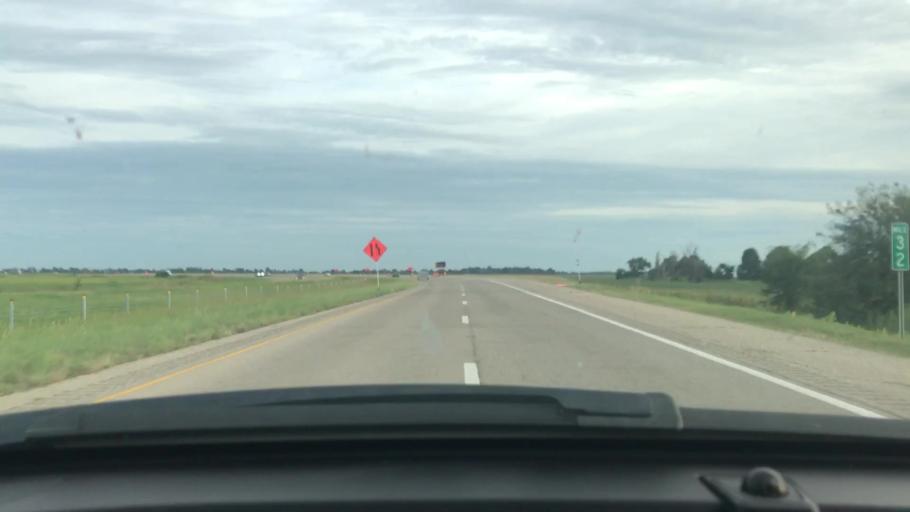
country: US
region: Arkansas
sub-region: Craighead County
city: Bay
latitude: 35.7202
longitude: -90.5801
